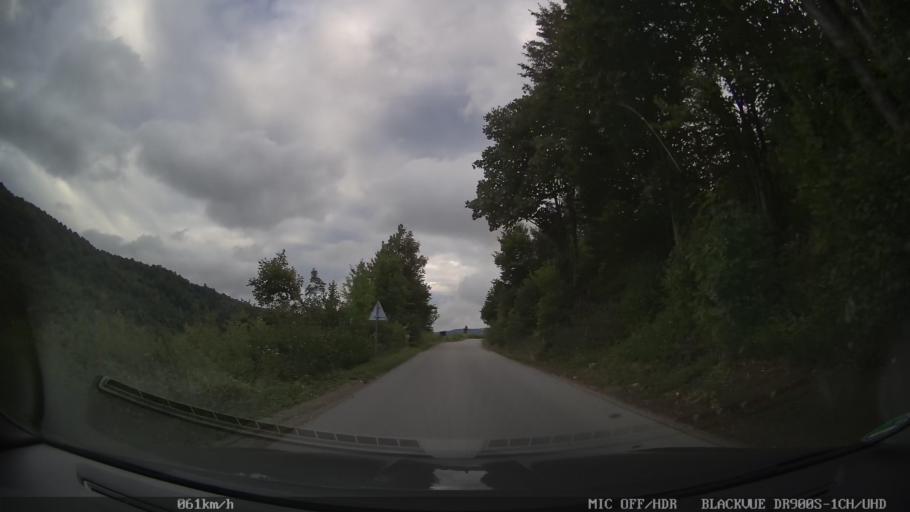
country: HR
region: Licko-Senjska
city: Jezerce
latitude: 44.9316
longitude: 15.6233
